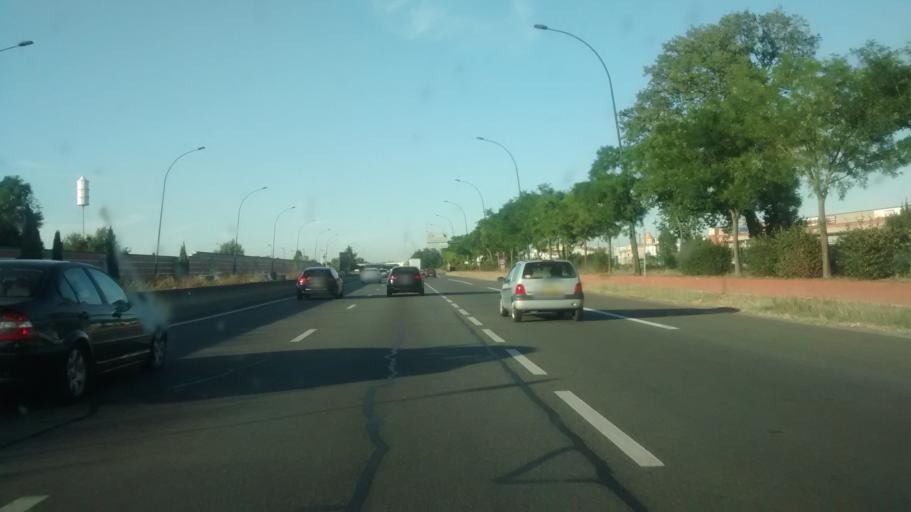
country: FR
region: Midi-Pyrenees
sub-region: Departement de la Haute-Garonne
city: Portet-sur-Garonne
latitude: 43.5500
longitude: 1.4061
